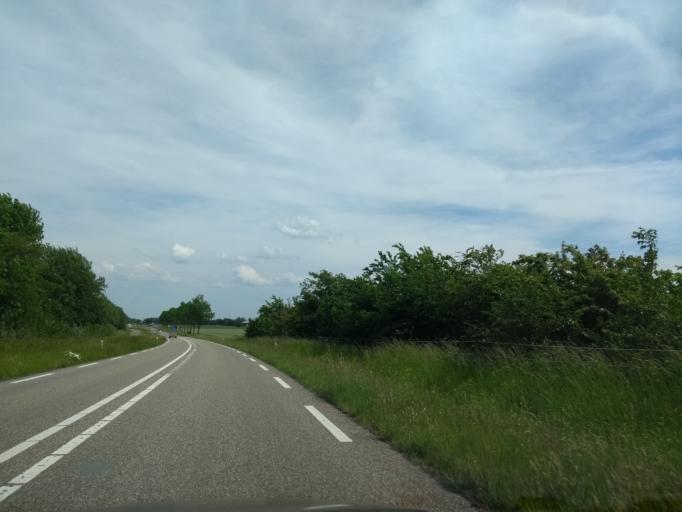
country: NL
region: Groningen
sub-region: Gemeente De Marne
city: Ulrum
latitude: 53.3656
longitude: 6.2984
